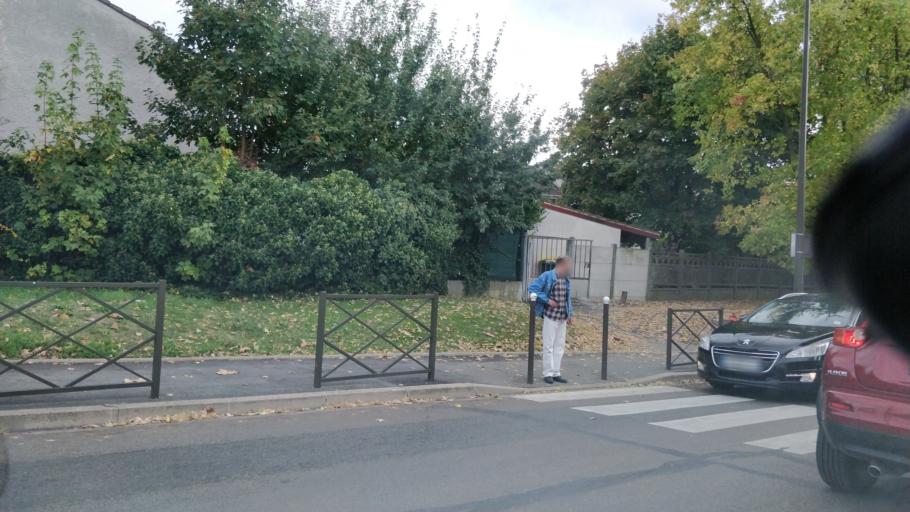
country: FR
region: Ile-de-France
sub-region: Departement de Seine-Saint-Denis
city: Clichy-sous-Bois
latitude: 48.9142
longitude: 2.5492
